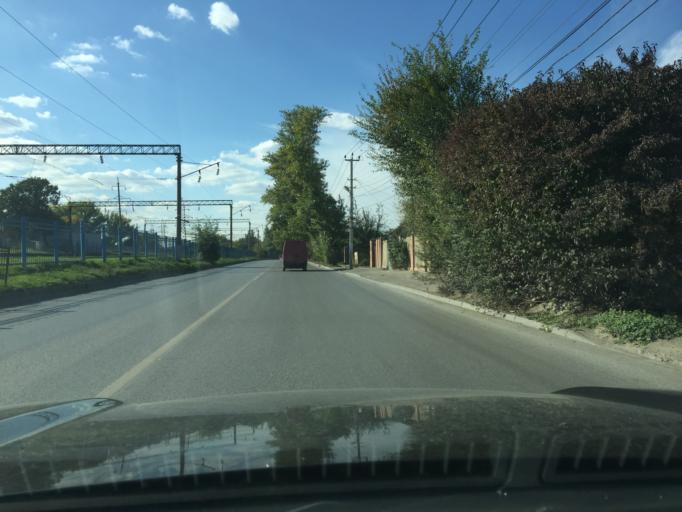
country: RU
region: Rostov
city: Rostov-na-Donu
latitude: 47.2460
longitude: 39.6836
